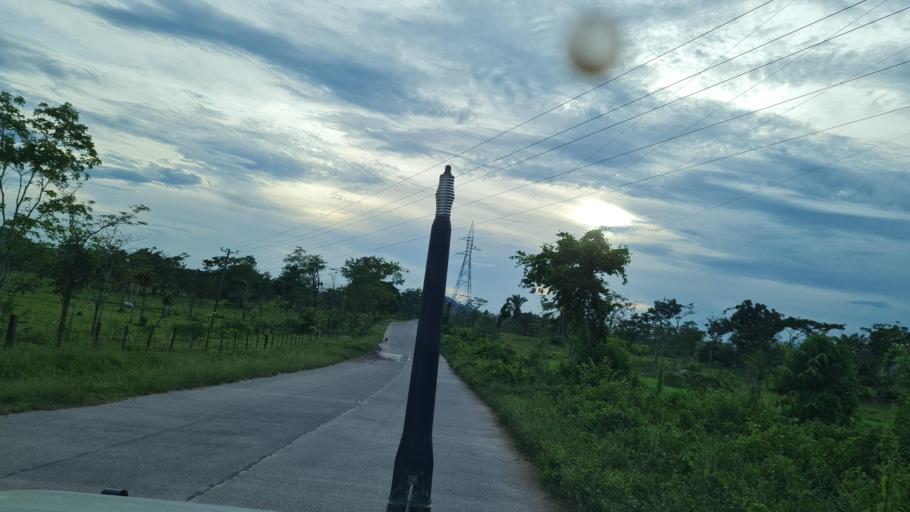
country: NI
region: Atlantico Norte (RAAN)
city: Siuna
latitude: 13.6830
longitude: -84.5836
